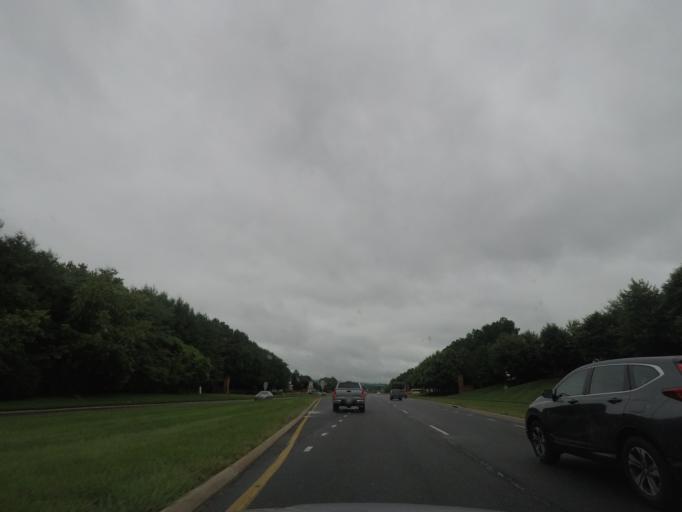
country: US
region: Virginia
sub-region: Prince William County
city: Haymarket
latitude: 38.8418
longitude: -77.6357
